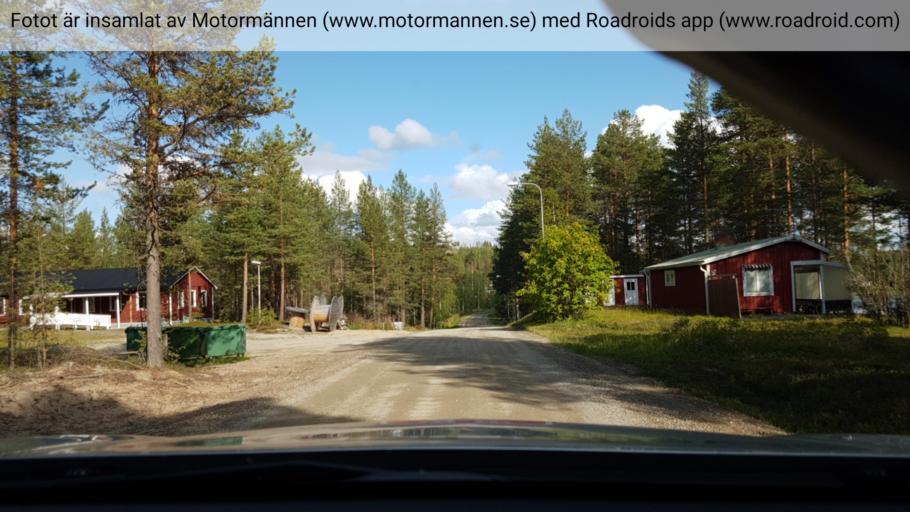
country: SE
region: Vaesterbotten
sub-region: Norsjo Kommun
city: Norsjoe
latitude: 64.6069
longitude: 19.1651
